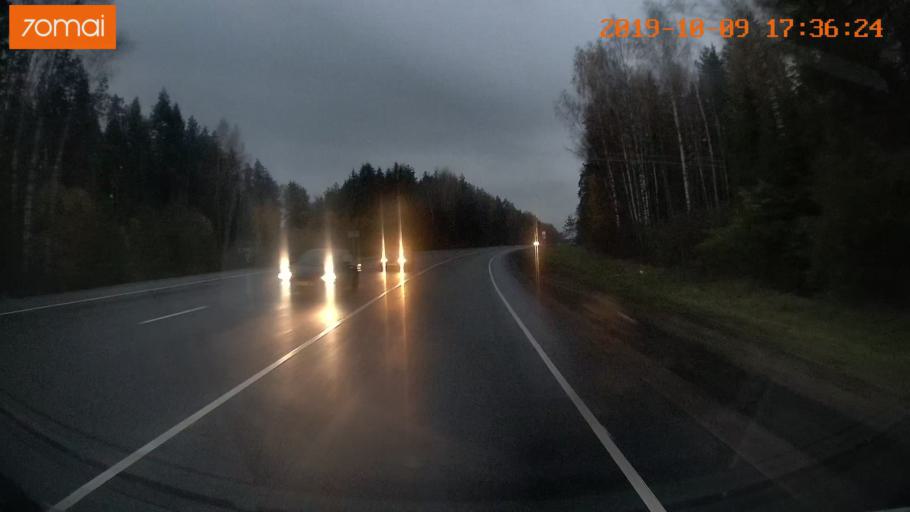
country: RU
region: Ivanovo
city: Bogorodskoye
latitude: 57.0790
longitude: 40.9976
